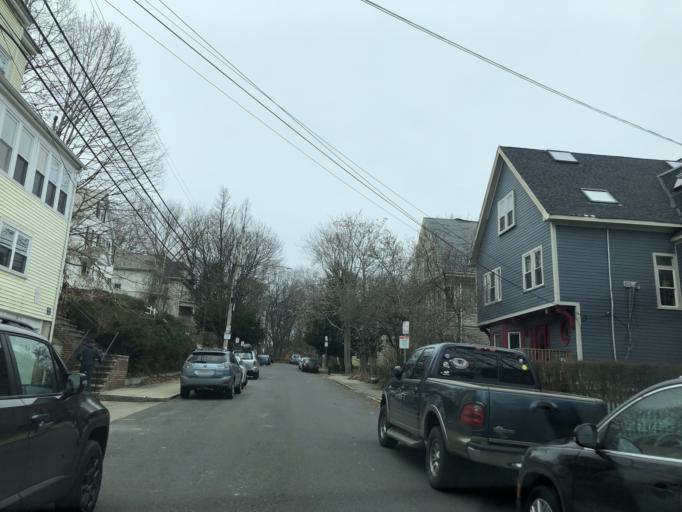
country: US
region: Massachusetts
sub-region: Norfolk County
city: Brookline
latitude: 42.3513
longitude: -71.1416
